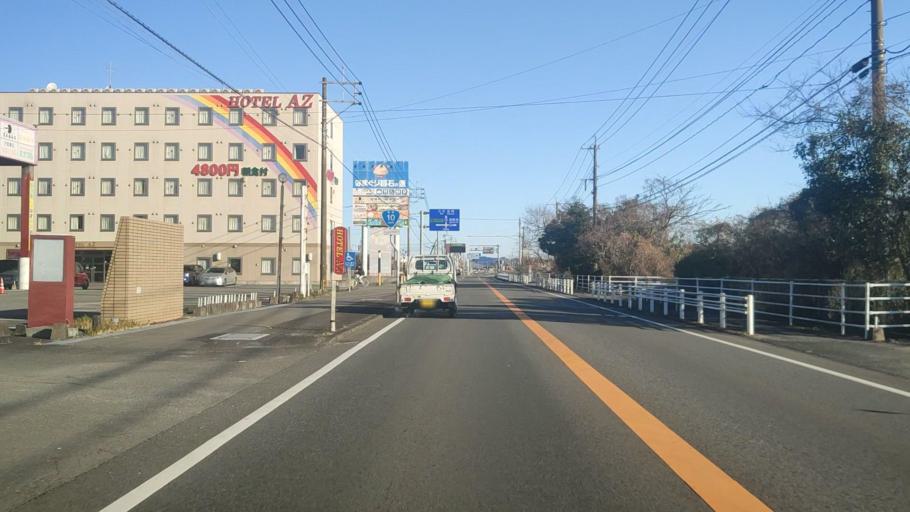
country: JP
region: Miyazaki
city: Nobeoka
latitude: 32.3935
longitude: 131.6284
